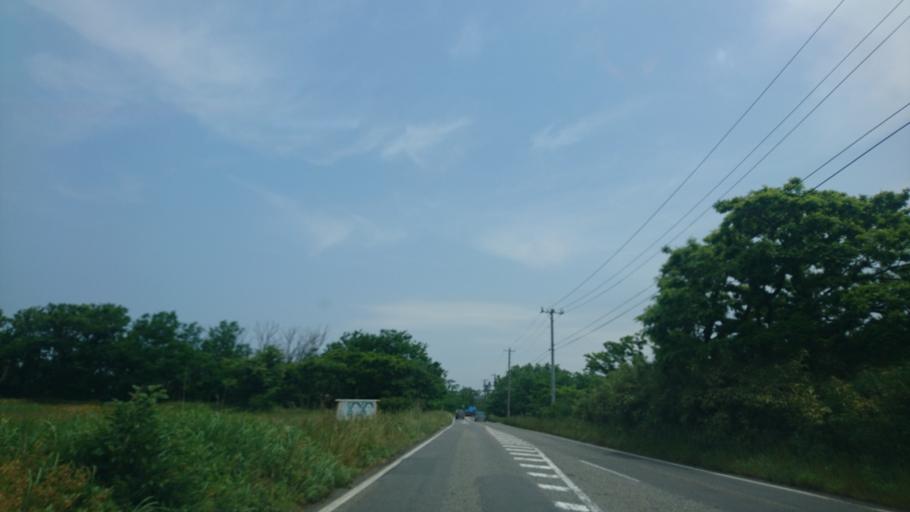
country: JP
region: Niigata
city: Shibata
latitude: 38.0385
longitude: 139.3036
